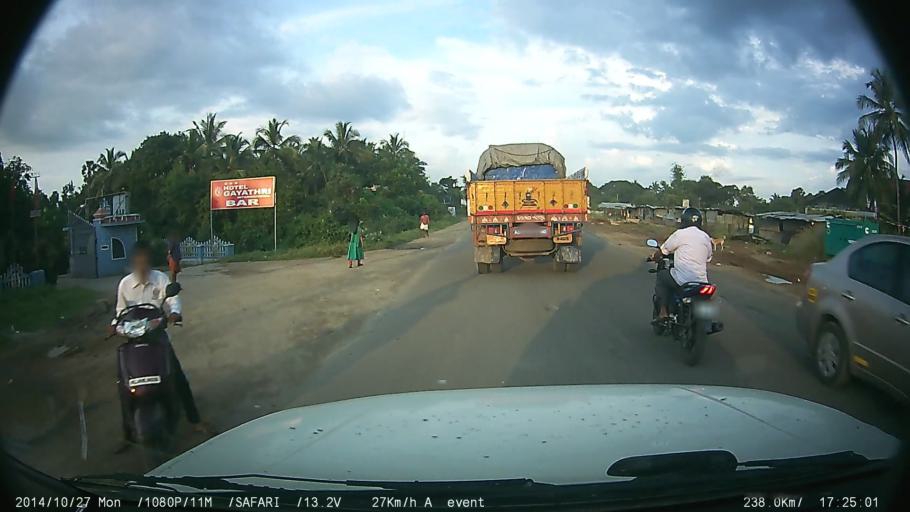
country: IN
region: Kerala
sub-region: Palakkad district
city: Palakkad
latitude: 10.6489
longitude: 76.5624
